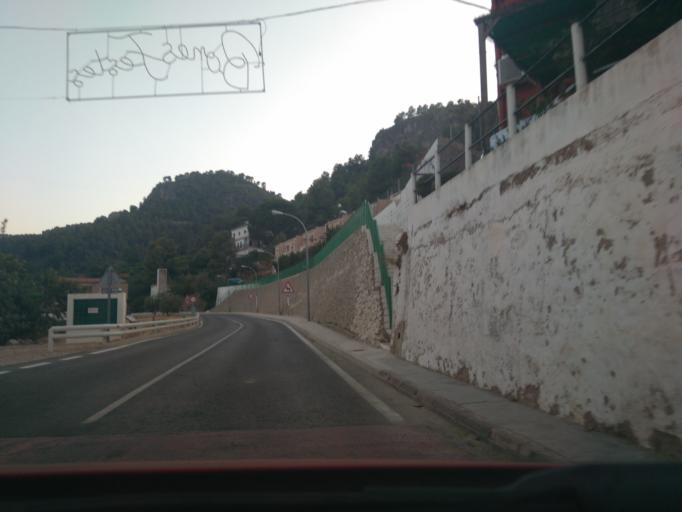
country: ES
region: Valencia
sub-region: Provincia de Valencia
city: Sumacarcer
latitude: 39.0914
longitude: -0.6290
